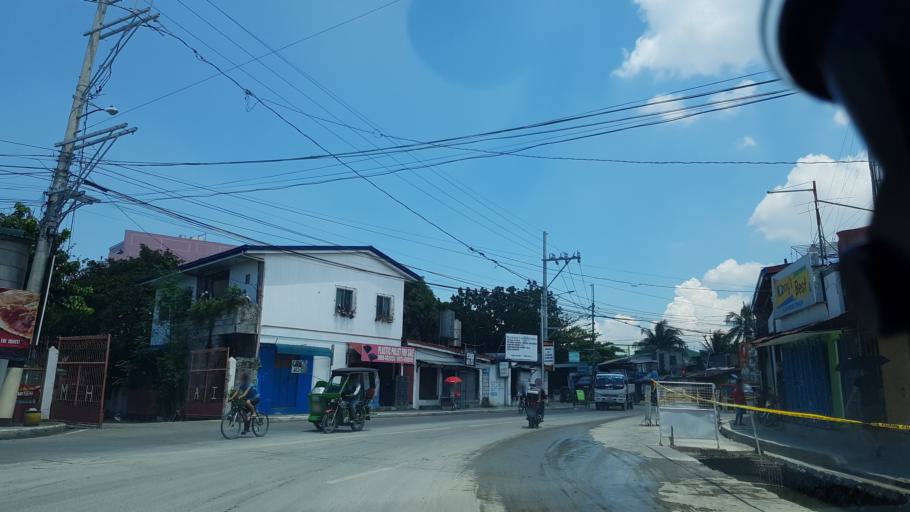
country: PH
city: Sambayanihan People's Village
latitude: 14.4623
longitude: 120.9949
